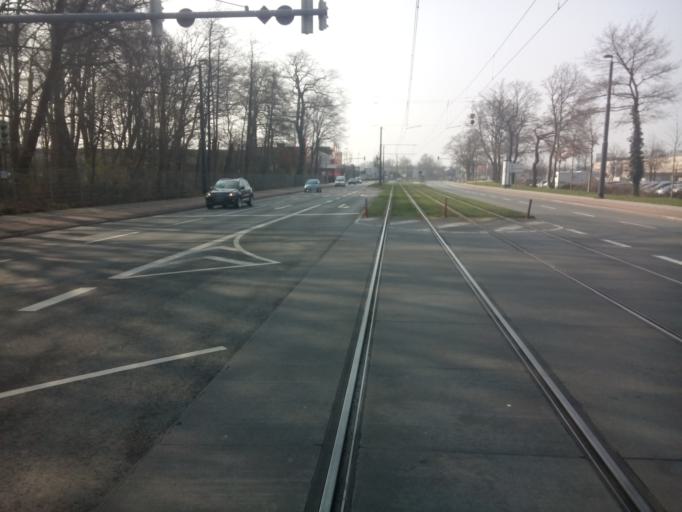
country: DE
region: Lower Saxony
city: Oyten
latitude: 53.0501
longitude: 8.9609
